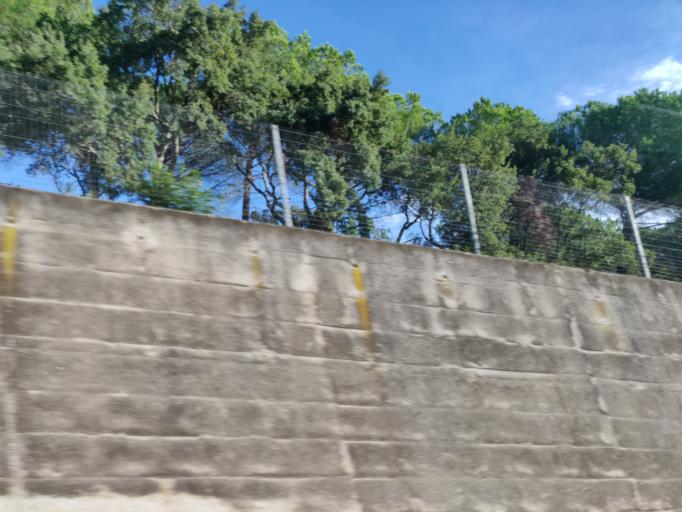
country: IT
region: Tuscany
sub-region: Provincia di Grosseto
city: Scarlino Scalo
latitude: 42.9639
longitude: 10.8496
